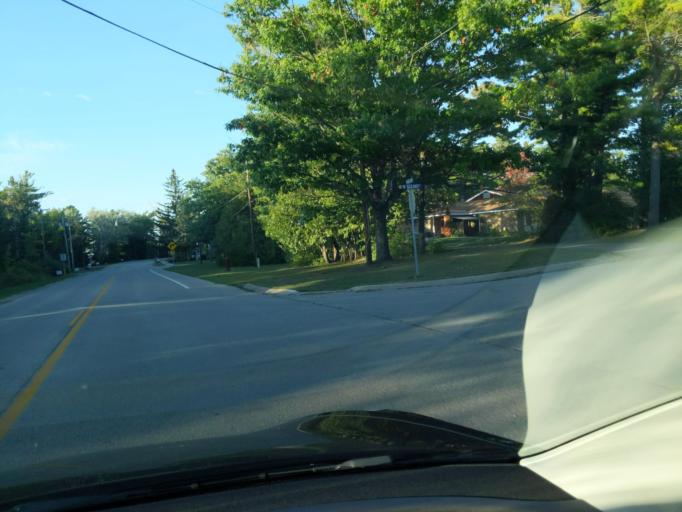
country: US
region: Michigan
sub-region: Antrim County
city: Elk Rapids
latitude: 44.8927
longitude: -85.4223
